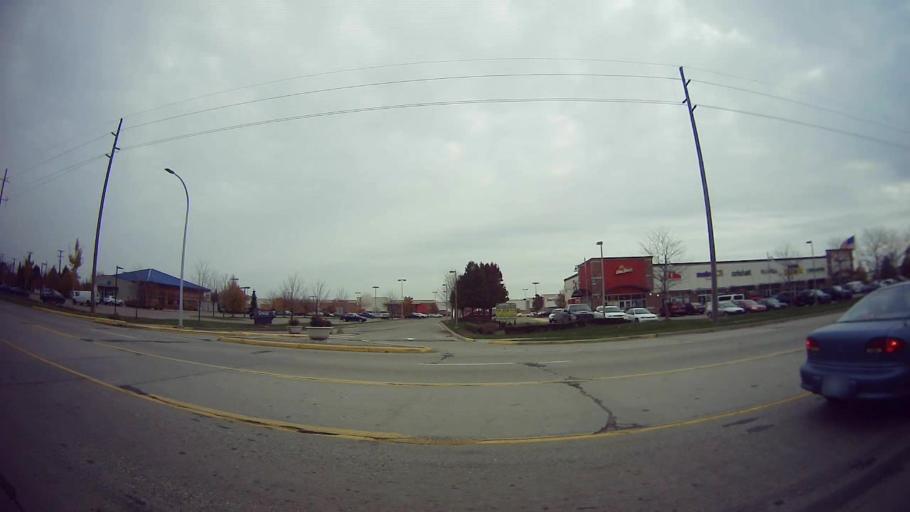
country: US
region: Michigan
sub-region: Oakland County
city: Madison Heights
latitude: 42.5032
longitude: -83.0856
